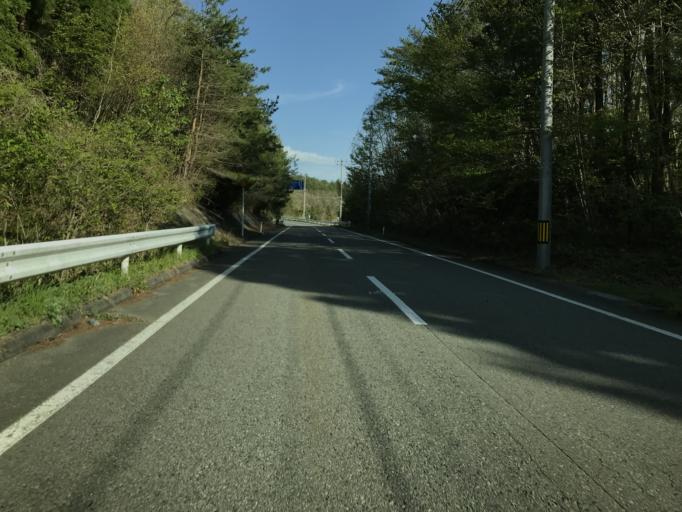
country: JP
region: Fukushima
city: Funehikimachi-funehiki
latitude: 37.5277
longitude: 140.7480
